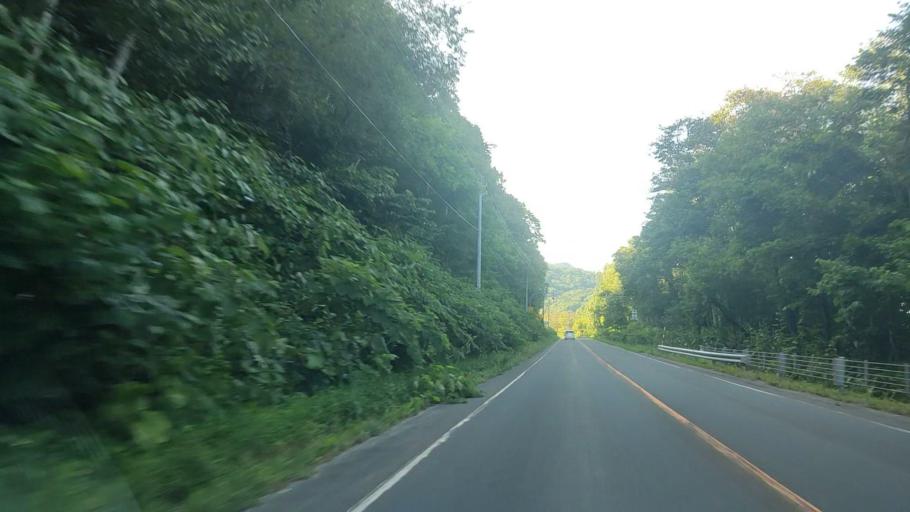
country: JP
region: Hokkaido
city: Nayoro
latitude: 44.7362
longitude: 142.1894
